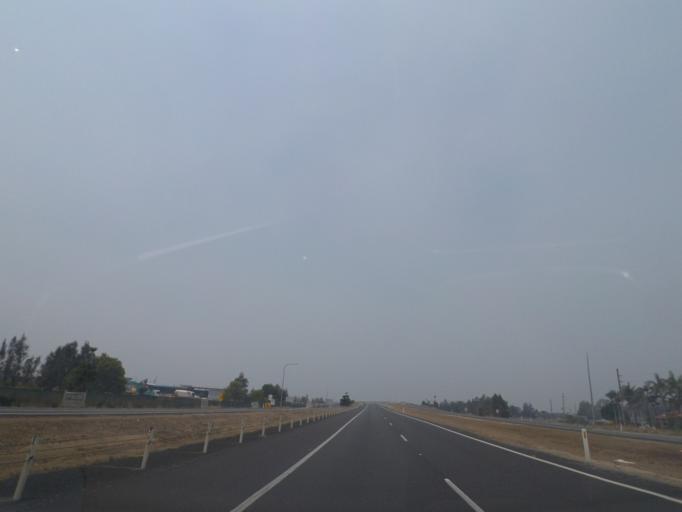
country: AU
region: New South Wales
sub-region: Ballina
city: Ballina
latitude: -28.8627
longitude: 153.5152
